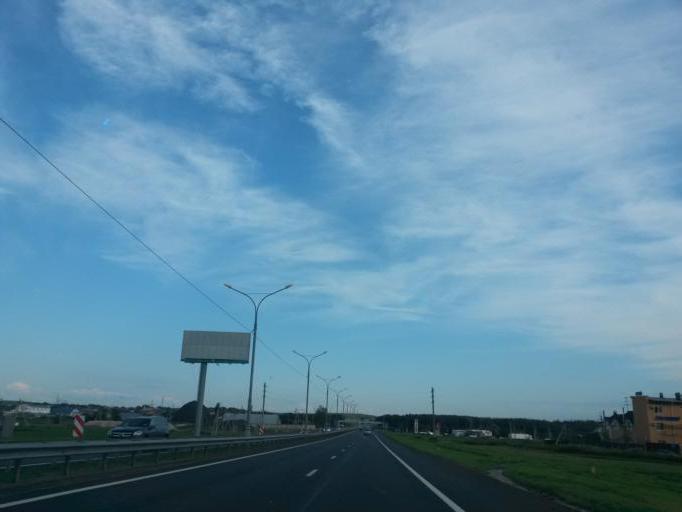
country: RU
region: Moskovskaya
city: Gorki-Leninskiye
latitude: 55.5003
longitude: 37.8400
